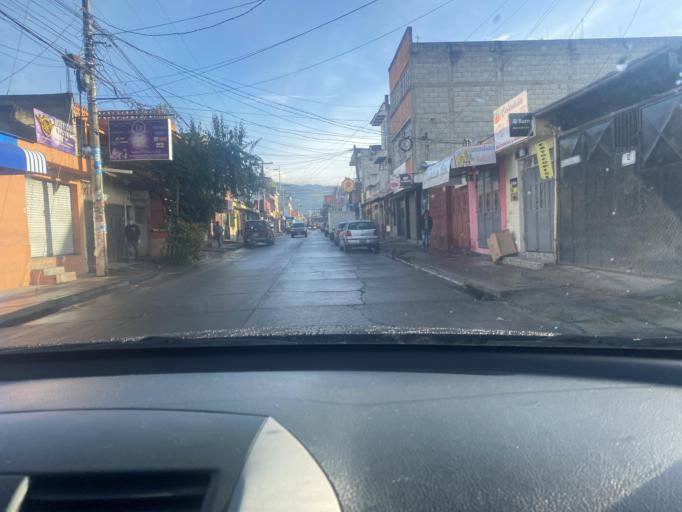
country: GT
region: Quetzaltenango
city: Olintepeque
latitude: 14.8607
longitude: -91.5204
